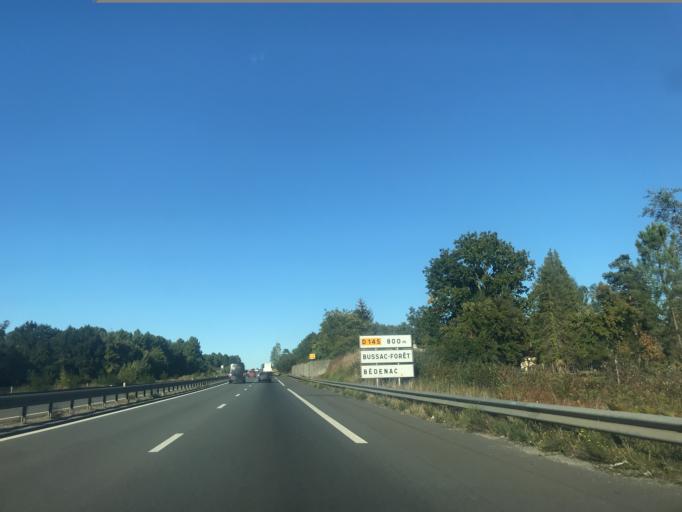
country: FR
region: Aquitaine
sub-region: Departement de la Gironde
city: Laruscade
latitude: 45.1775
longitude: -0.3276
